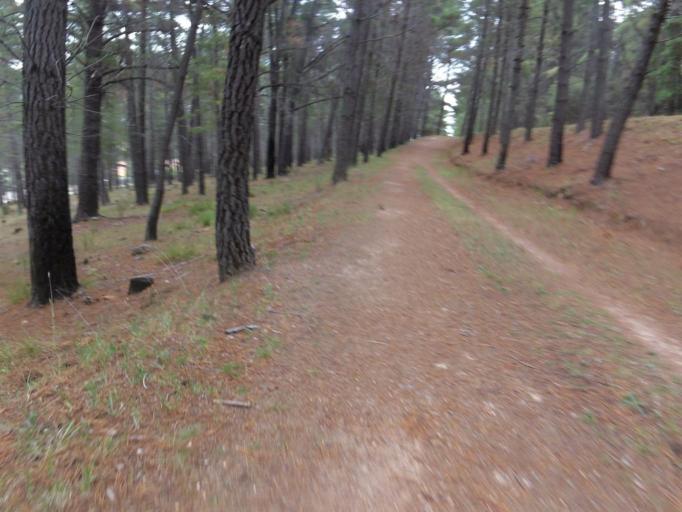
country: AU
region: Australian Capital Territory
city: Macarthur
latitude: -35.3652
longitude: 149.1141
